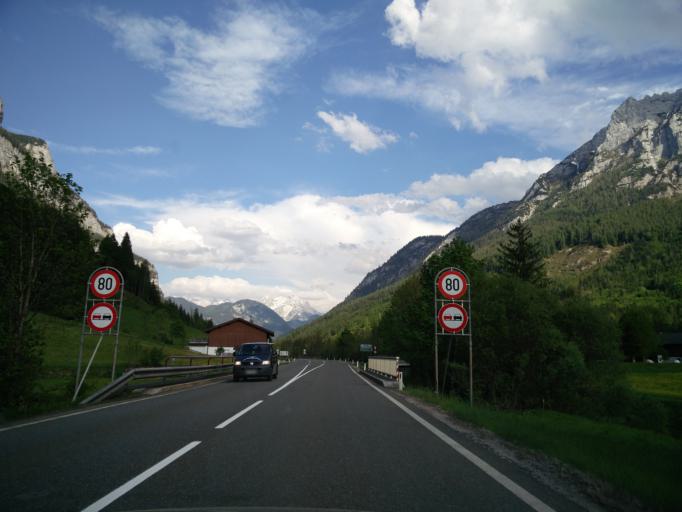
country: AT
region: Tyrol
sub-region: Politischer Bezirk Kitzbuhel
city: Waidring
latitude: 47.5840
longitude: 12.6260
